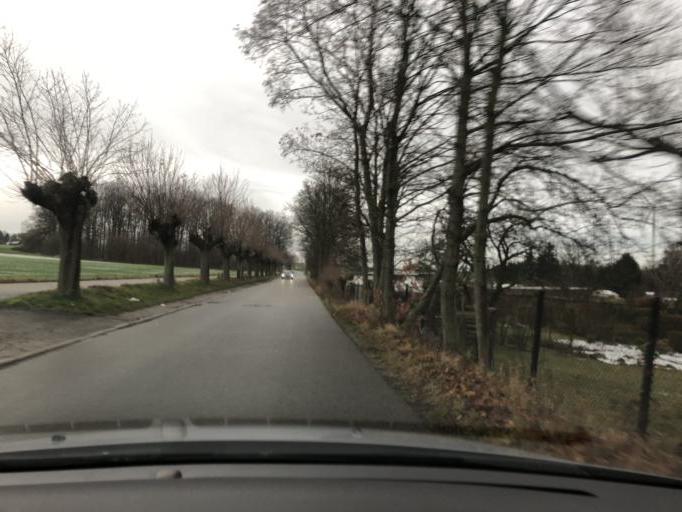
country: DE
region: Saxony
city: Limbach-Oberfrohna
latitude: 50.8577
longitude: 12.7296
